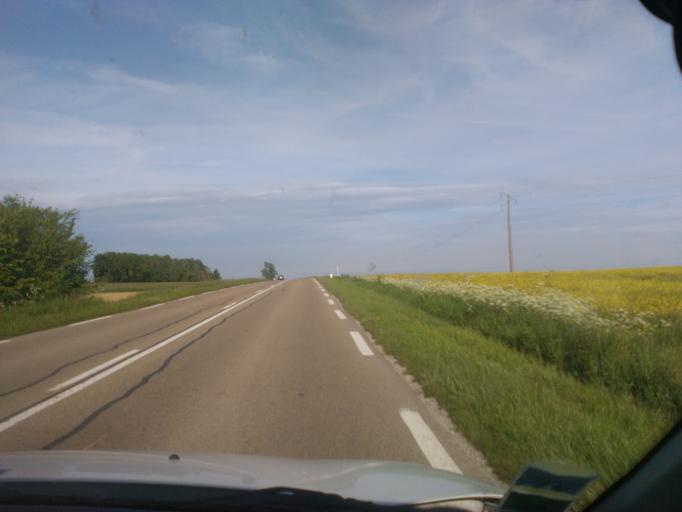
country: FR
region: Champagne-Ardenne
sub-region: Departement de l'Aube
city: Lusigny-sur-Barse
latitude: 48.2425
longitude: 4.3555
